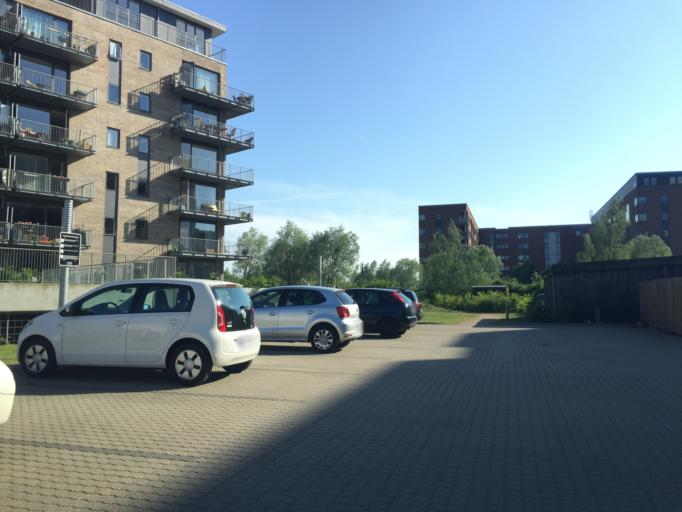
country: DK
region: Capital Region
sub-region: Kobenhavn
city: Copenhagen
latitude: 55.6616
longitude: 12.5741
